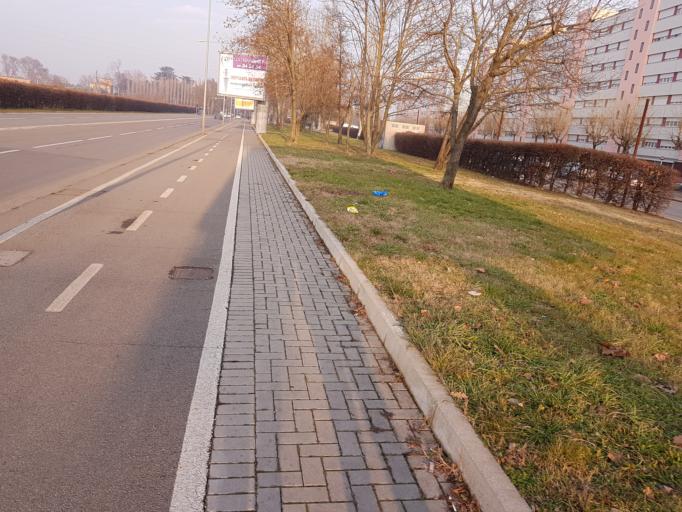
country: IT
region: Emilia-Romagna
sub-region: Provincia di Bologna
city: Quarto Inferiore
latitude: 44.5133
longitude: 11.3875
